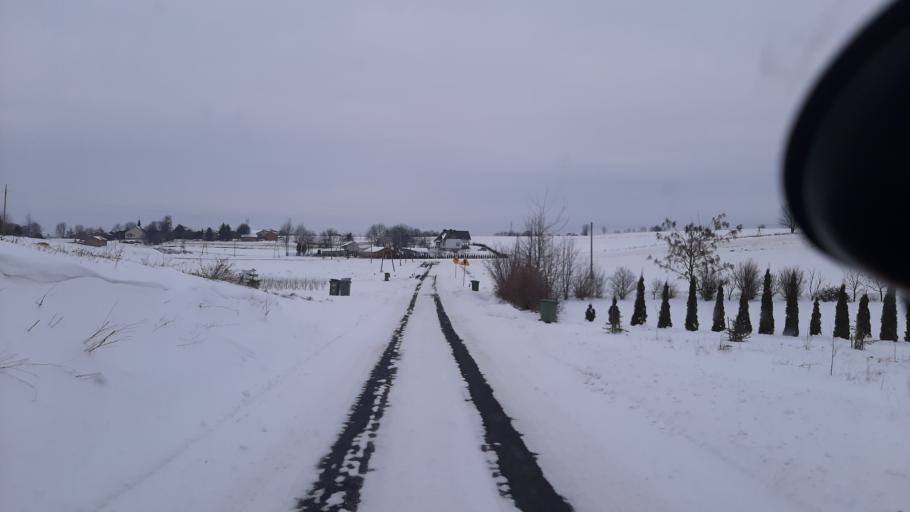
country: PL
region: Lublin Voivodeship
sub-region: Powiat lubelski
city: Garbow
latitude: 51.3381
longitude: 22.2942
